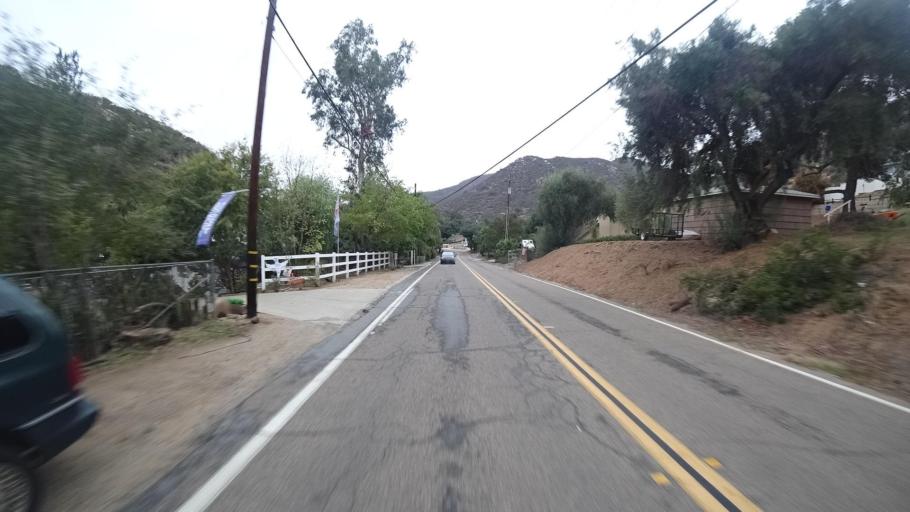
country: US
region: California
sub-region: San Diego County
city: Harbison Canyon
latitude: 32.8140
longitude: -116.8387
